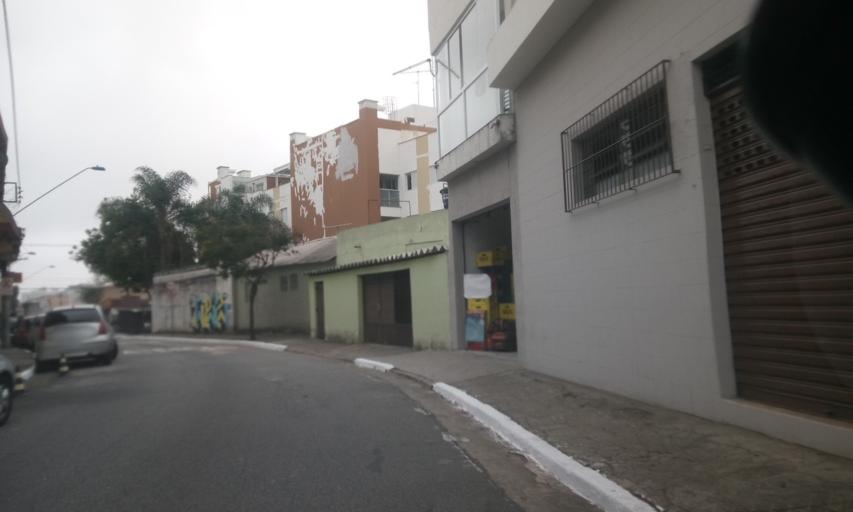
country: BR
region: Sao Paulo
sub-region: Sao Caetano Do Sul
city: Sao Caetano do Sul
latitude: -23.6374
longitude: -46.5693
